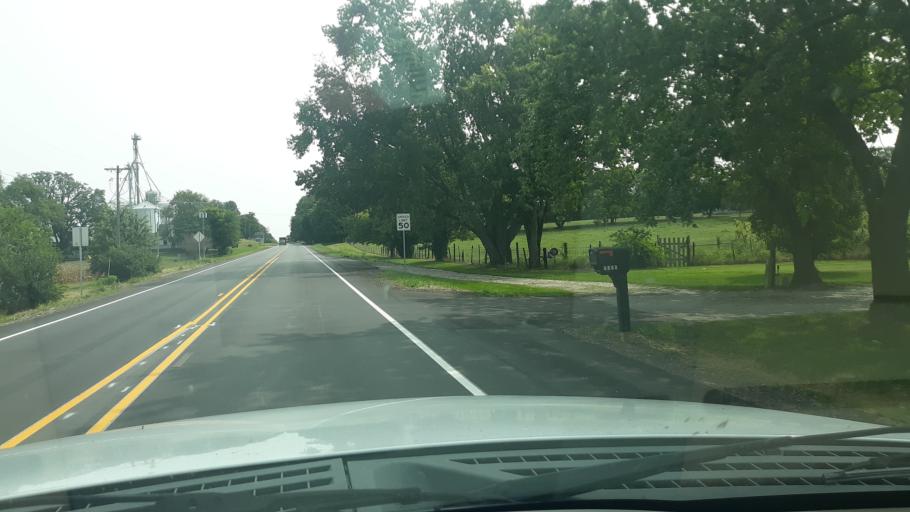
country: US
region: Indiana
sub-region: Gibson County
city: Princeton
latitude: 38.3556
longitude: -87.6247
